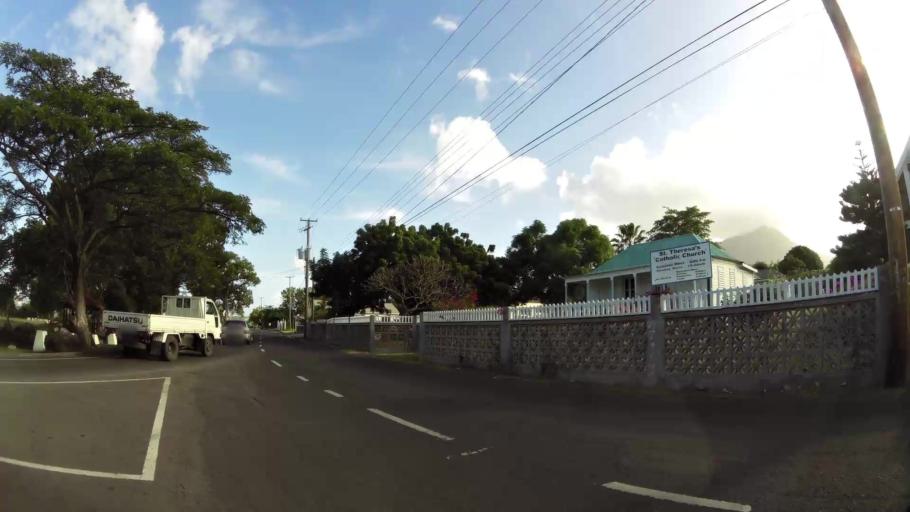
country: KN
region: Saint Paul Charlestown
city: Charlestown
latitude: 17.1433
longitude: -62.6291
